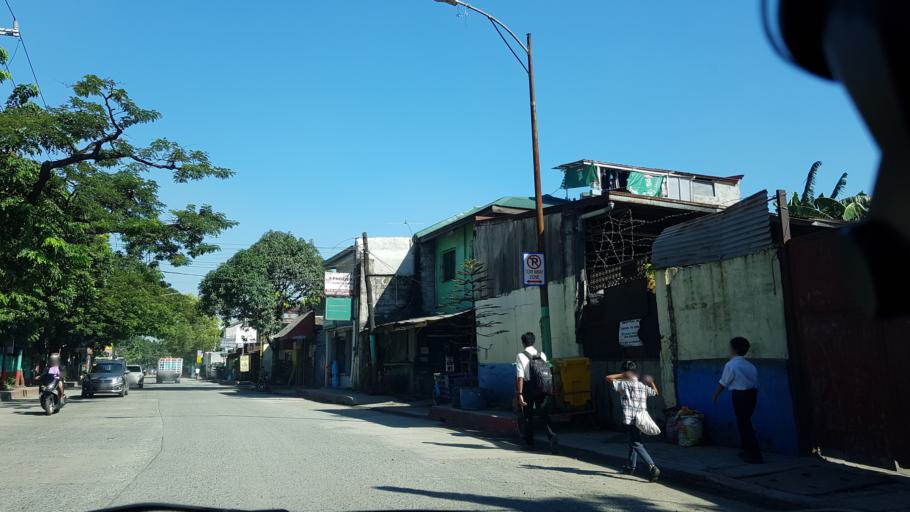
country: PH
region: Calabarzon
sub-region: Province of Rizal
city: Pateros
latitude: 14.5584
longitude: 121.0964
